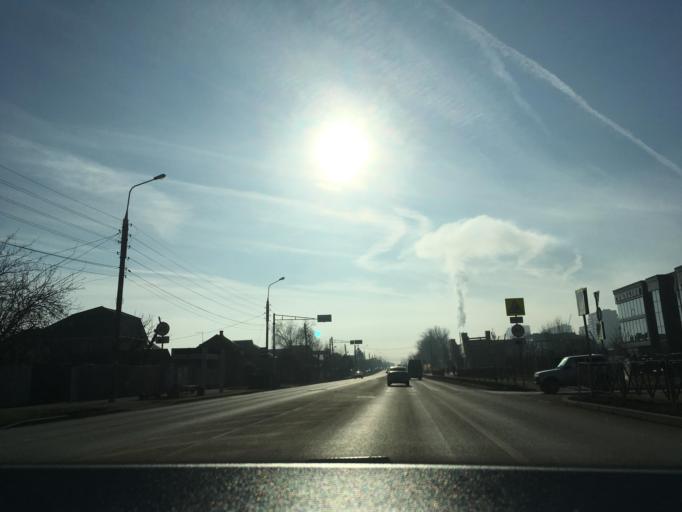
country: RU
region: Krasnodarskiy
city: Krasnodar
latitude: 45.0999
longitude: 39.0132
